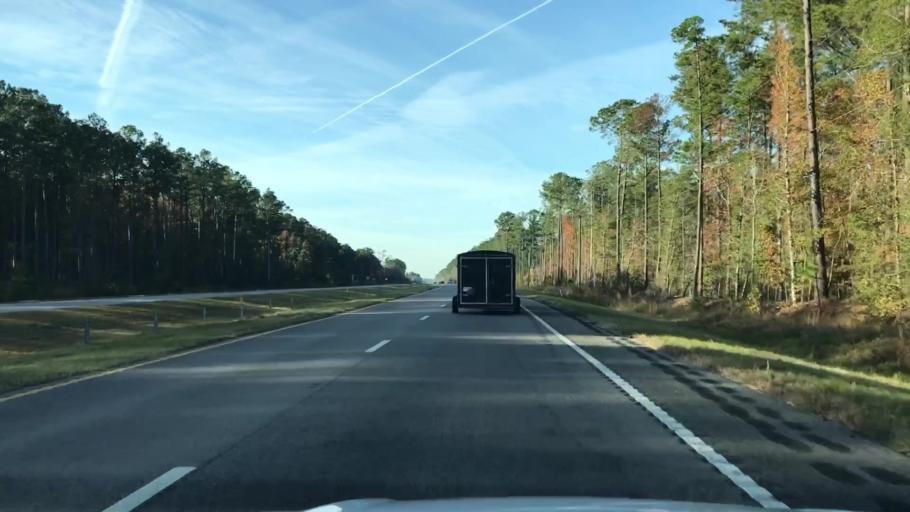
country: US
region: South Carolina
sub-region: Colleton County
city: Walterboro
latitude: 32.7058
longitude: -80.6140
